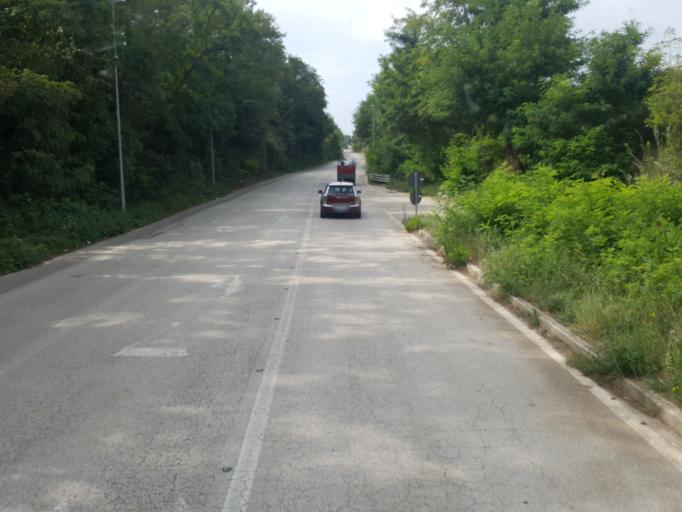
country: IT
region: Campania
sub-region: Provincia di Caserta
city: Pignataro Maggiore
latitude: 41.1773
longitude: 14.1531
